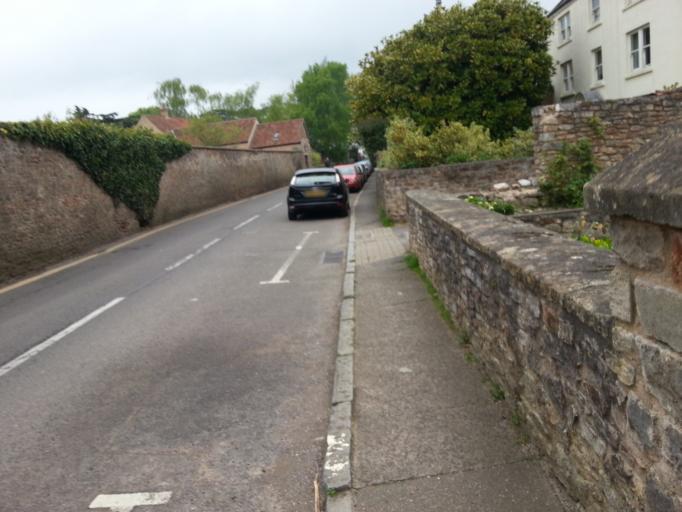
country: GB
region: England
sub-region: Somerset
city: Wells
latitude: 51.2103
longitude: -2.6406
